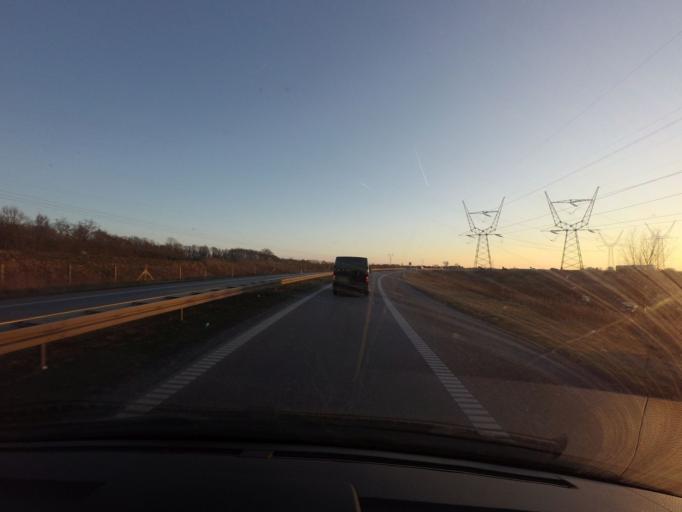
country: DK
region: South Denmark
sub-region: Odense Kommune
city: Neder Holluf
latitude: 55.3483
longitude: 10.4592
